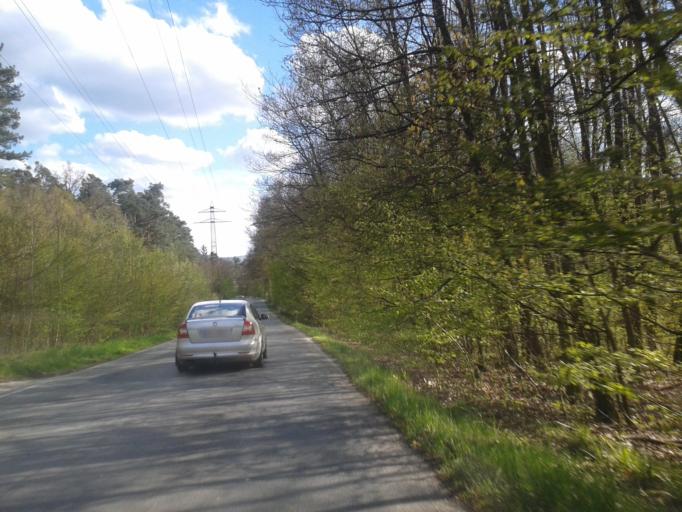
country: CZ
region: Central Bohemia
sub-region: Okres Beroun
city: Beroun
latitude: 49.9880
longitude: 14.0859
